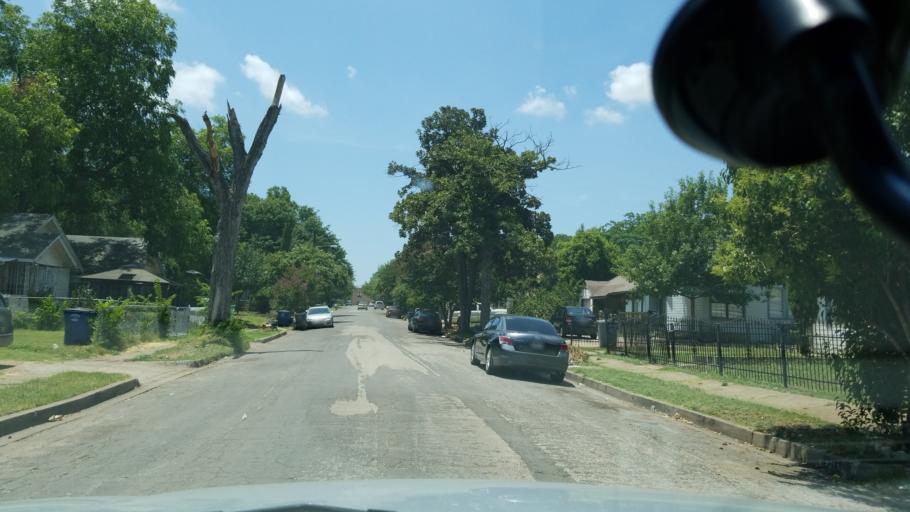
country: US
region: Texas
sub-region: Dallas County
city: Cockrell Hill
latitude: 32.7330
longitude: -96.8644
